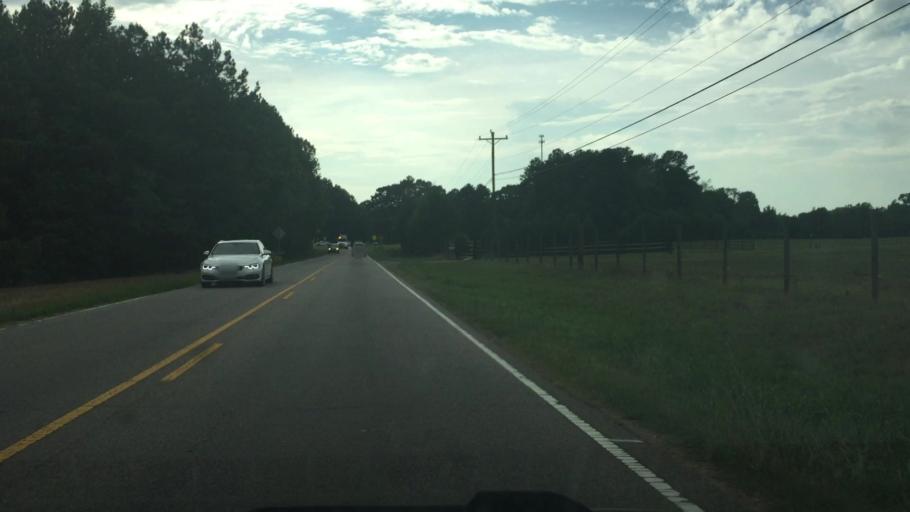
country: US
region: North Carolina
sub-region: Gaston County
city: Davidson
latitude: 35.4891
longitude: -80.7614
